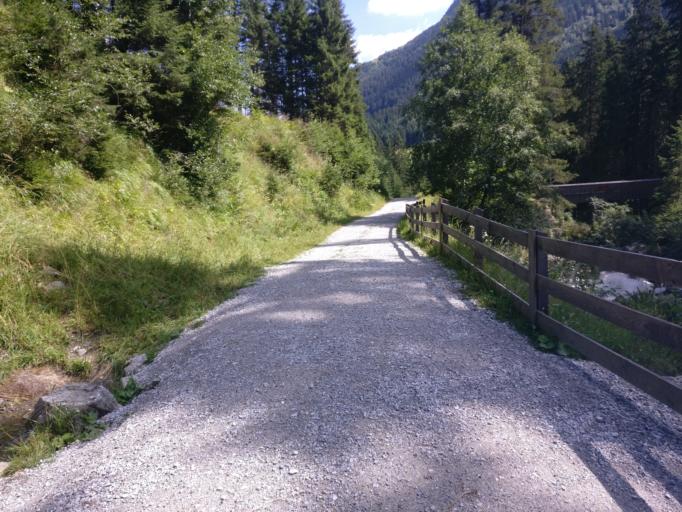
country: AT
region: Tyrol
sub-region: Politischer Bezirk Innsbruck Land
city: Neustift im Stubaital
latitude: 47.0278
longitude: 11.2186
